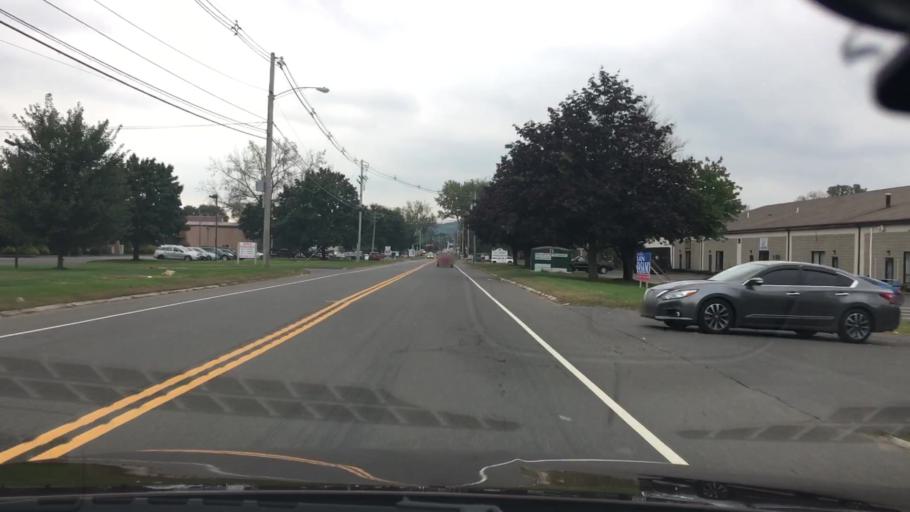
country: US
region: Connecticut
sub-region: New Haven County
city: Wallingford
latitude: 41.4862
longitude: -72.8132
